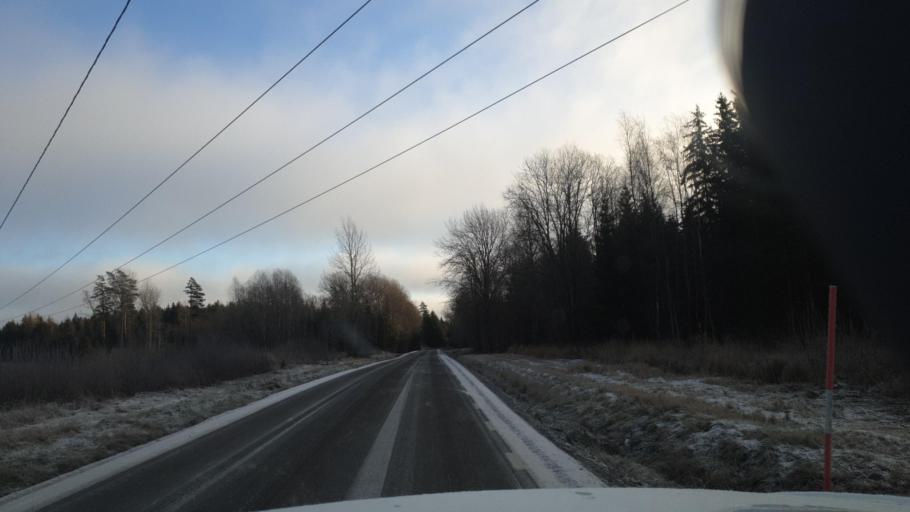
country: SE
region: Vaermland
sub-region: Karlstads Kommun
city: Valberg
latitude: 59.4135
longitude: 13.1646
